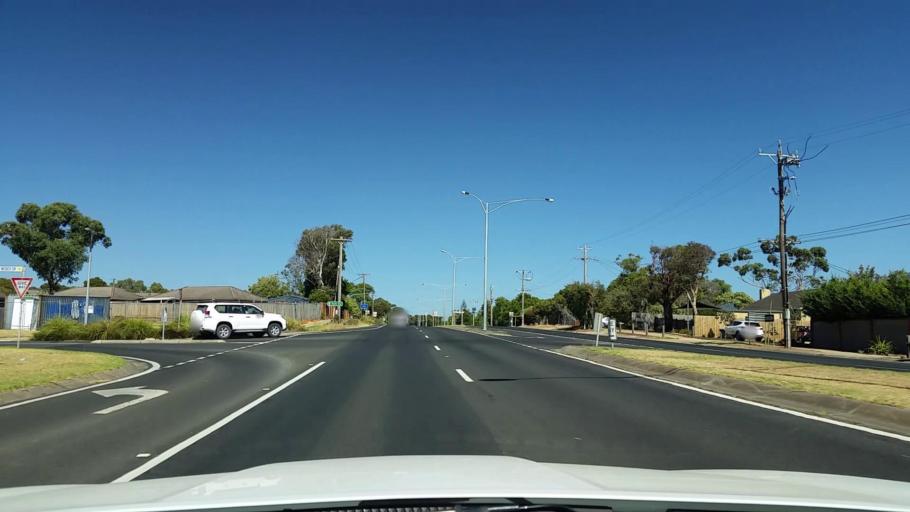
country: AU
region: Victoria
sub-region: Mornington Peninsula
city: Mornington
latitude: -38.2401
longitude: 145.0364
